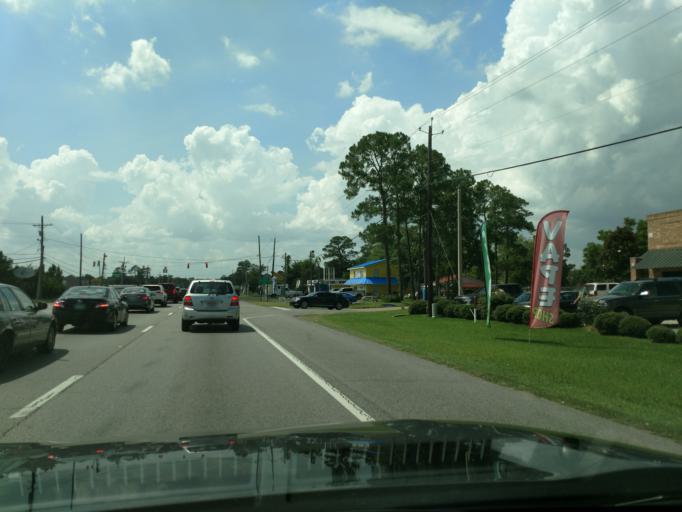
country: US
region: Mississippi
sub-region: Jackson County
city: Gulf Hills
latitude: 30.4377
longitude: -88.8326
